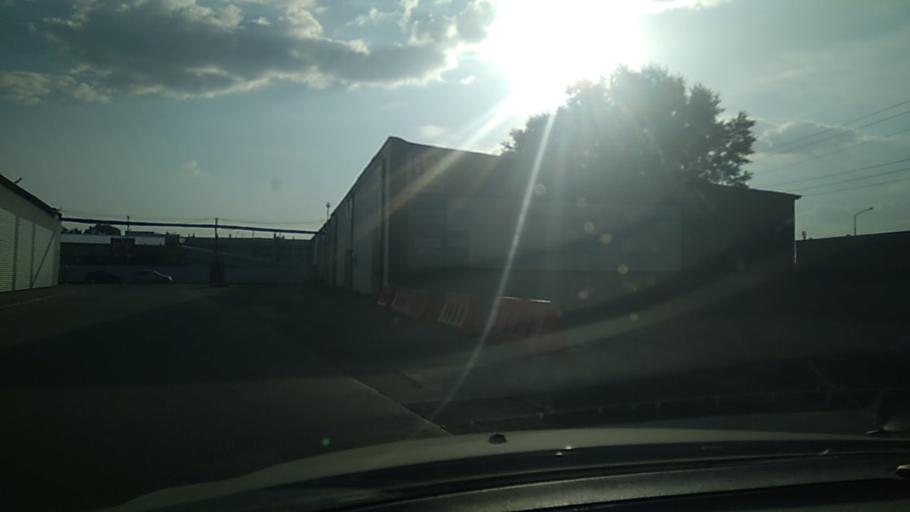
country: RU
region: Sverdlovsk
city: Yekaterinburg
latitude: 56.8178
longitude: 60.6505
